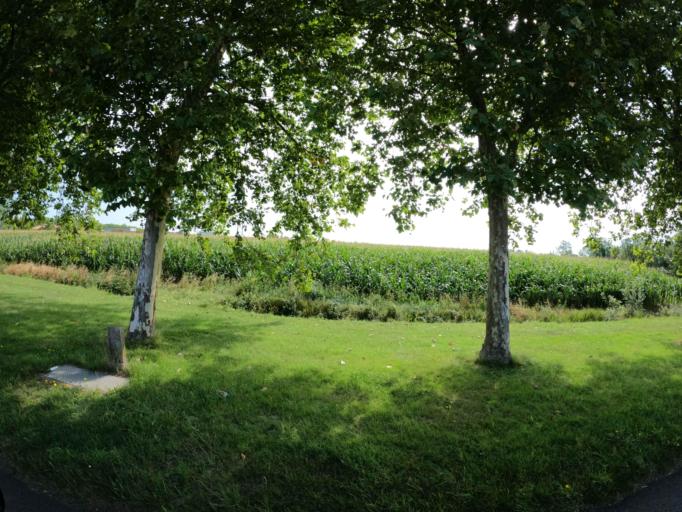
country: FR
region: Pays de la Loire
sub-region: Departement de la Vendee
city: Triaize
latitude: 46.3608
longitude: -1.2418
